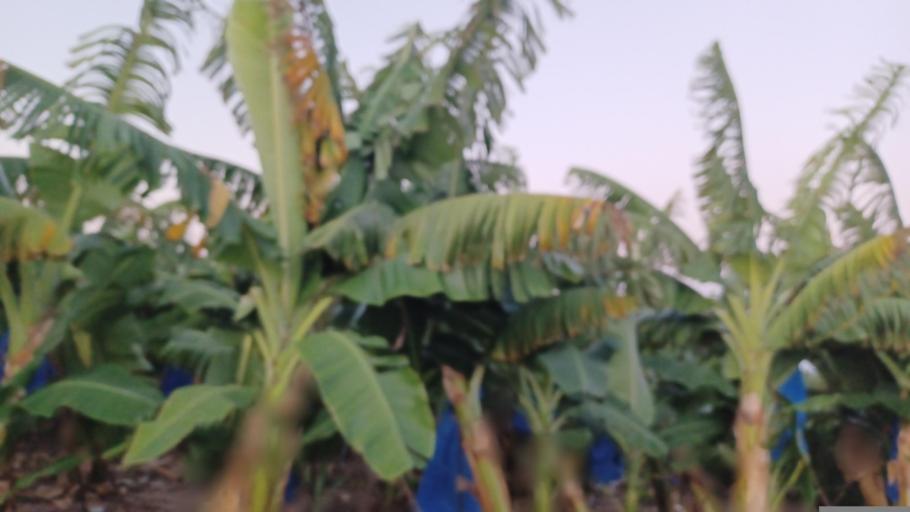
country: CY
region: Pafos
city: Pegeia
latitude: 34.8640
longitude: 32.3682
